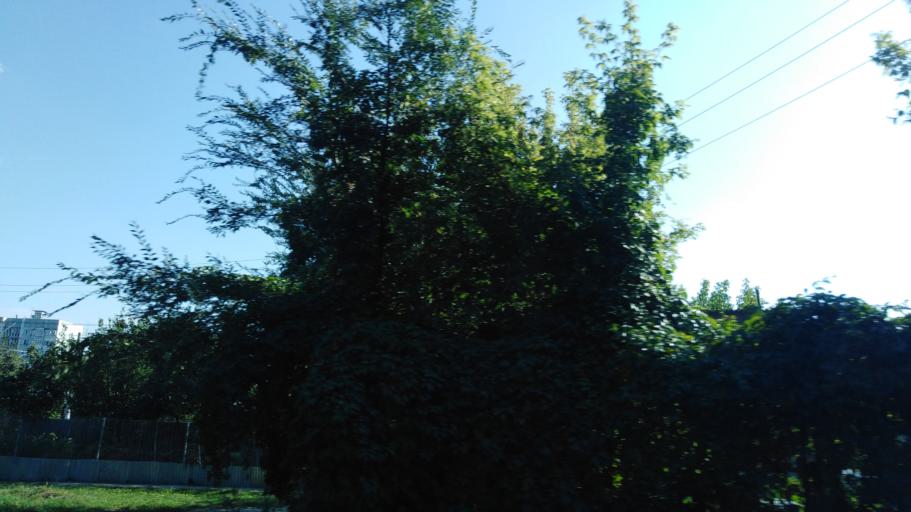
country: RU
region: Stavropol'skiy
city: Svobody
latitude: 44.0385
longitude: 43.0407
